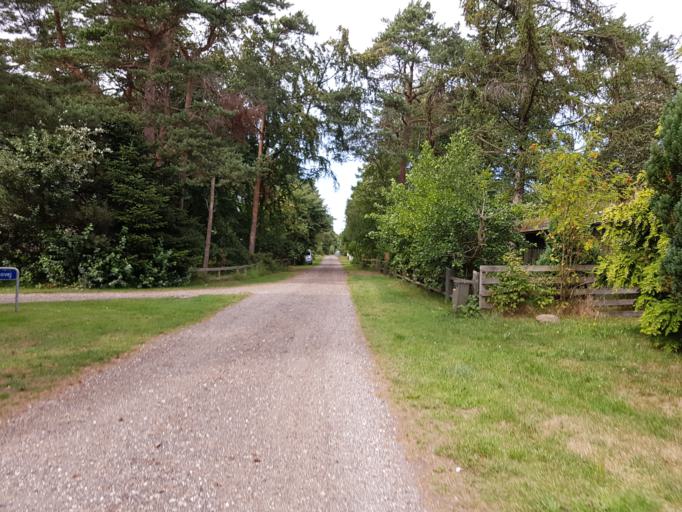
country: DK
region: Zealand
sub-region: Guldborgsund Kommune
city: Nykobing Falster
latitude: 54.5925
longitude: 11.9686
